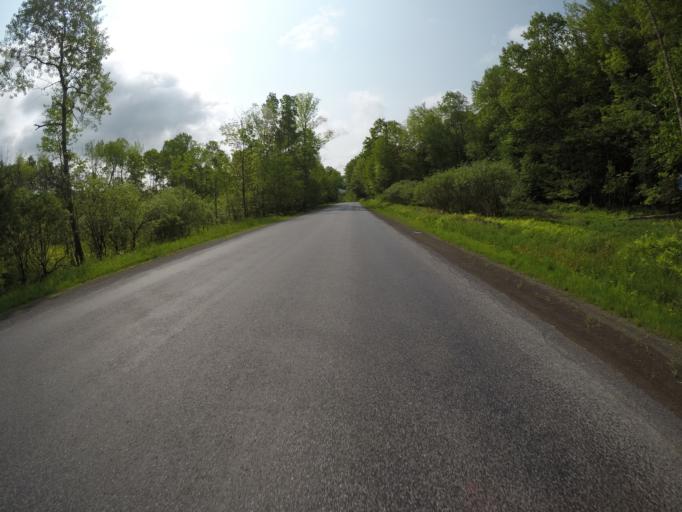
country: US
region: New York
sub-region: Delaware County
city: Stamford
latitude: 42.1614
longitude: -74.6615
